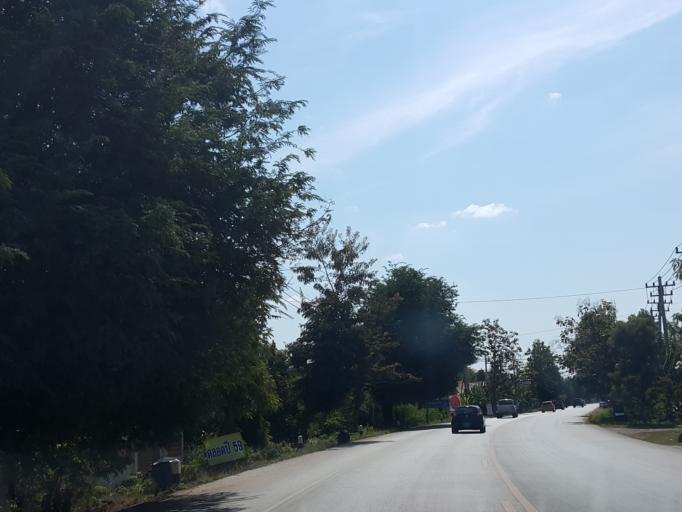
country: TH
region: Sukhothai
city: Sawankhalok
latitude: 17.2862
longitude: 99.8440
